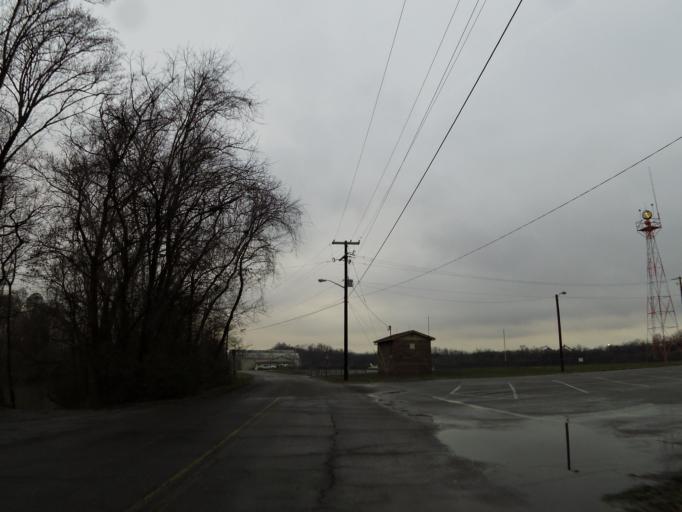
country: US
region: Tennessee
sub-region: Knox County
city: Knoxville
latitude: 35.9614
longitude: -83.8734
